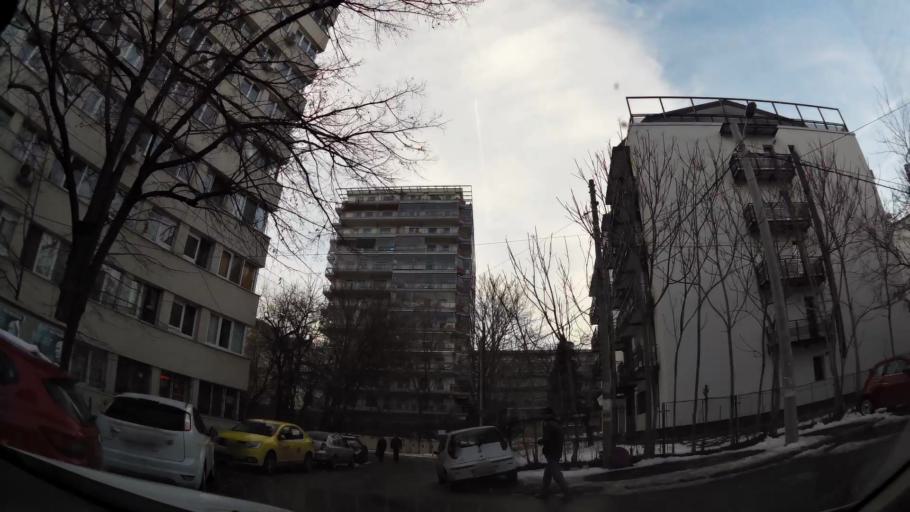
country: RO
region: Bucuresti
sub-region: Municipiul Bucuresti
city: Bucharest
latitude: 44.4224
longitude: 26.1396
